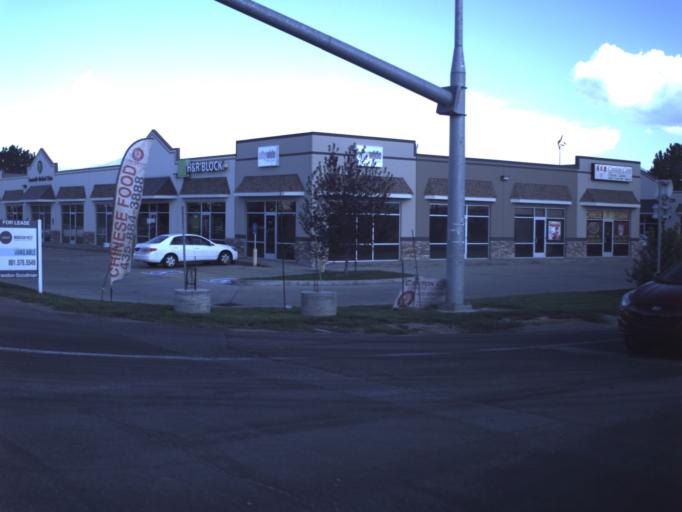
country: US
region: Utah
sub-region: Tooele County
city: Grantsville
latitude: 40.5996
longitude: -112.4260
